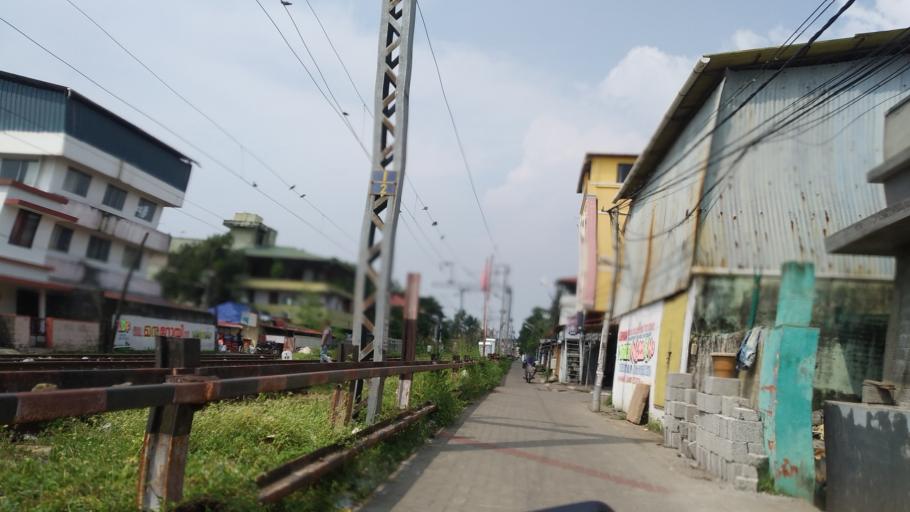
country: IN
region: Kerala
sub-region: Ernakulam
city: Cochin
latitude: 9.9602
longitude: 76.2931
